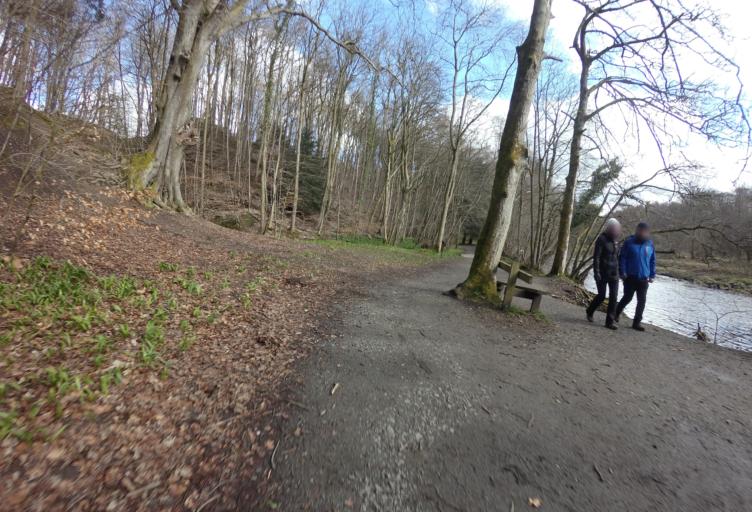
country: GB
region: Scotland
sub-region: West Lothian
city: East Calder
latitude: 55.9031
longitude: -3.4630
